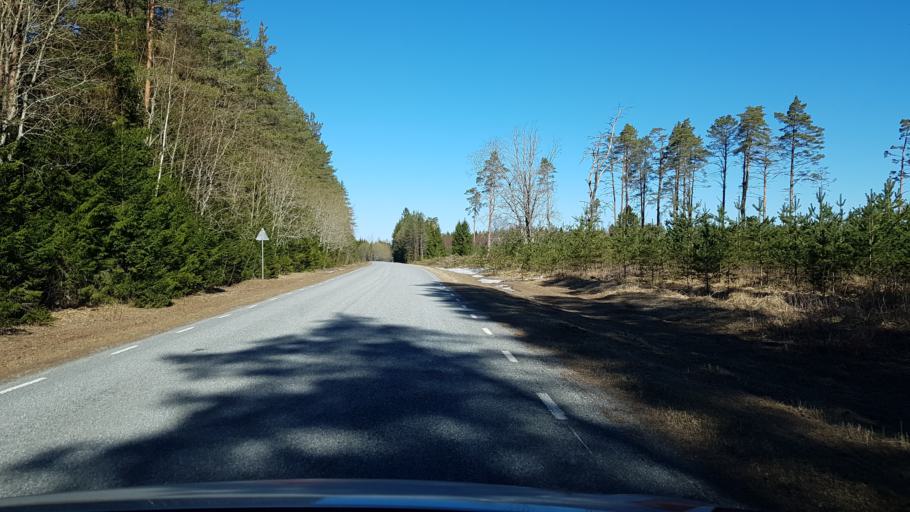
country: EE
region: Laeaene-Virumaa
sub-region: Haljala vald
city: Haljala
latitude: 59.4956
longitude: 26.2431
